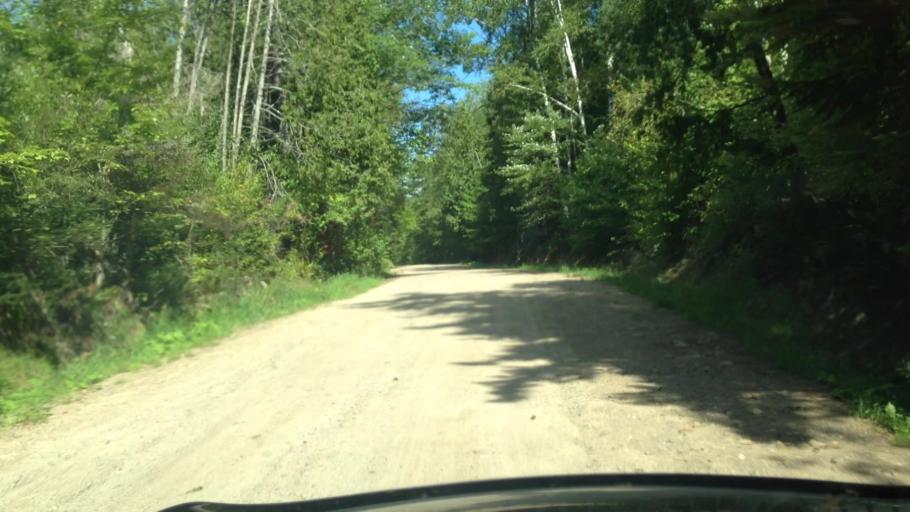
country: CA
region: Quebec
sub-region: Laurentides
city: Brownsburg-Chatham
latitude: 45.9213
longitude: -74.5806
